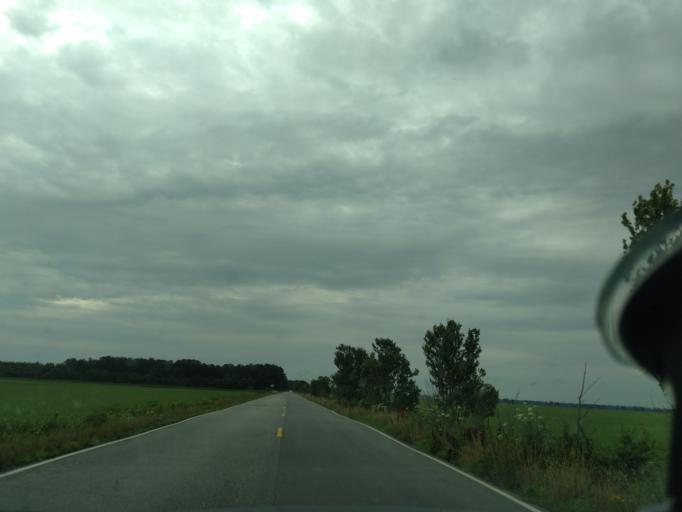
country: US
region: North Carolina
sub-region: Washington County
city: Plymouth
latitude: 35.8337
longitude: -76.5285
